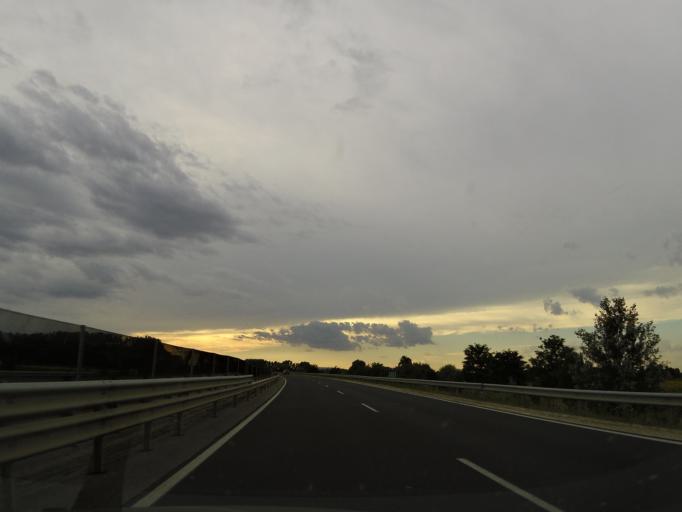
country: HU
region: Pest
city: Vecses
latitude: 47.4114
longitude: 19.2942
